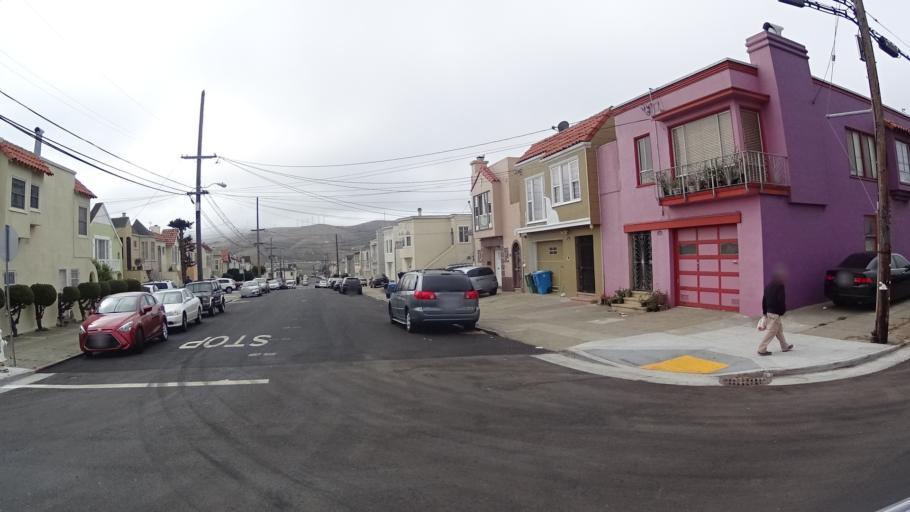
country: US
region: California
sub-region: San Mateo County
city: Brisbane
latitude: 37.7109
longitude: -122.4061
